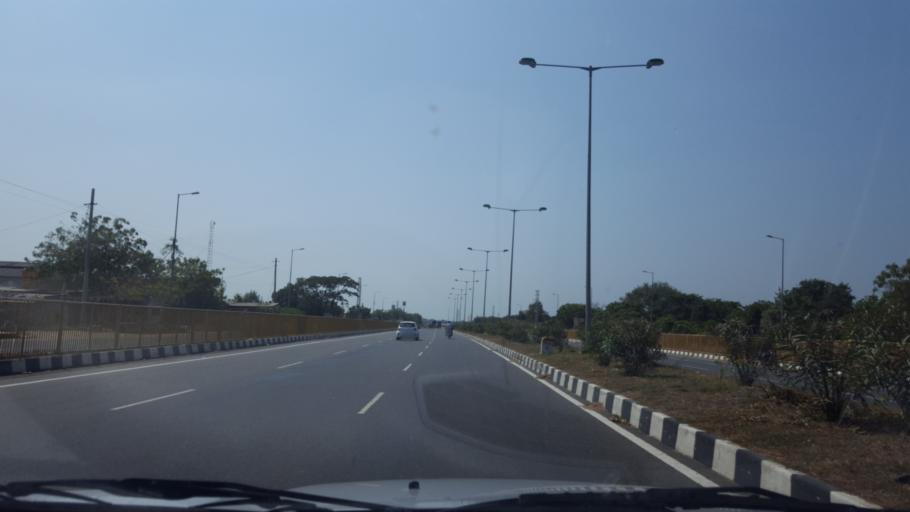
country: IN
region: Andhra Pradesh
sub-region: Prakasam
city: pedda nakkalapalem
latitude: 15.9552
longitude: 80.0881
